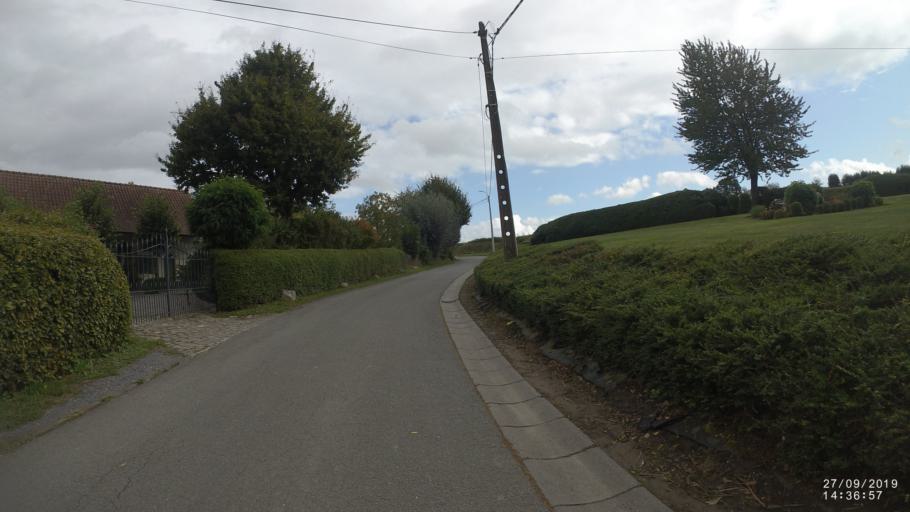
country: BE
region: Flanders
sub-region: Provincie Oost-Vlaanderen
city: Zingem
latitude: 50.8666
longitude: 3.6733
